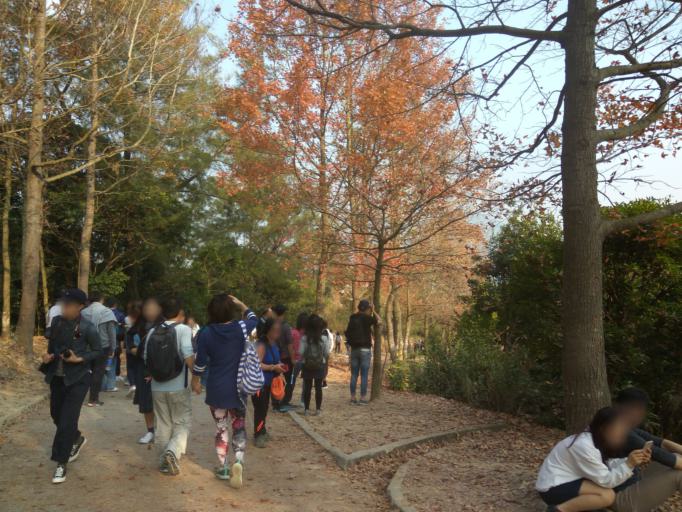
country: HK
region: Yuen Long
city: Yuen Long Kau Hui
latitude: 22.3979
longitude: 114.0377
